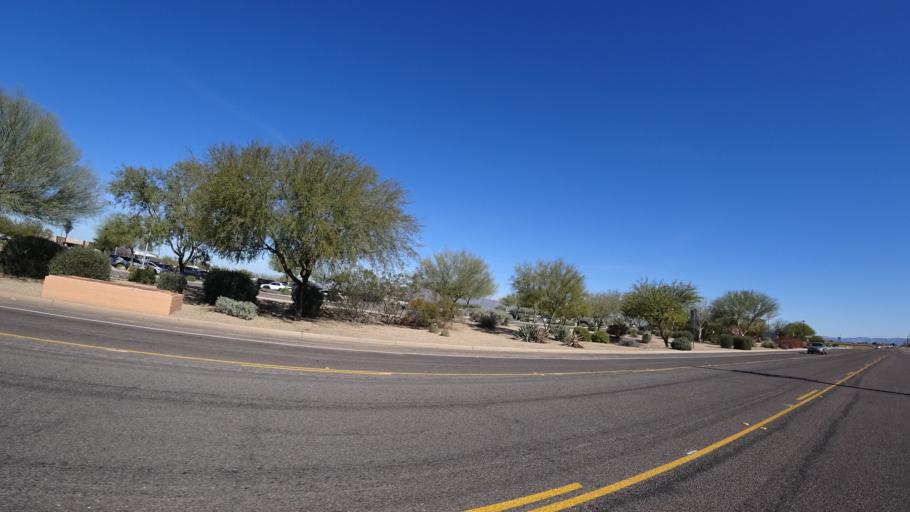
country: US
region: Arizona
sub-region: Maricopa County
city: Scottsdale
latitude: 33.5094
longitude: -111.8804
